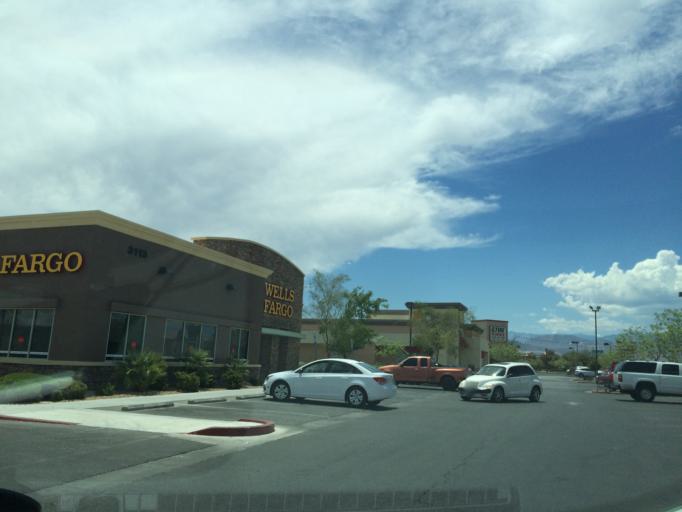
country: US
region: Nevada
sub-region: Clark County
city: North Las Vegas
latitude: 36.2613
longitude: -115.1823
